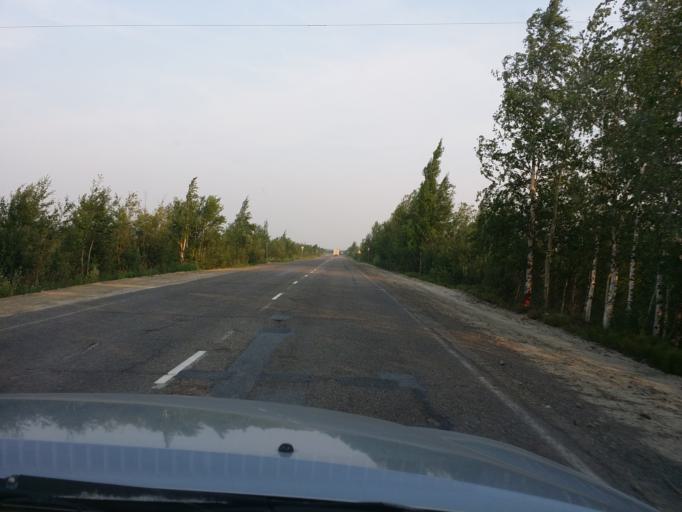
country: RU
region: Khanty-Mansiyskiy Avtonomnyy Okrug
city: Nizhnevartovsk
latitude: 61.1875
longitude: 76.5615
